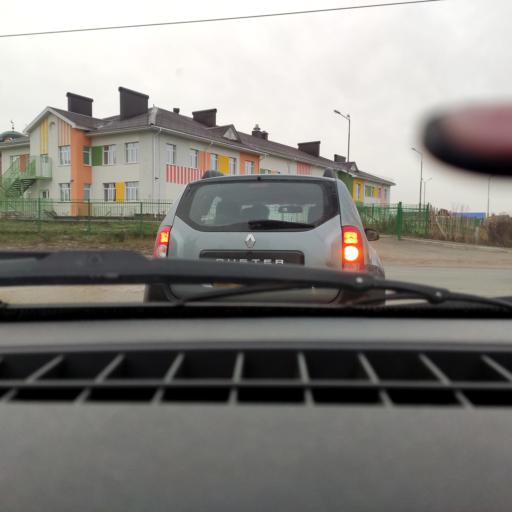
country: RU
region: Bashkortostan
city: Ufa
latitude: 54.8254
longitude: 56.1813
